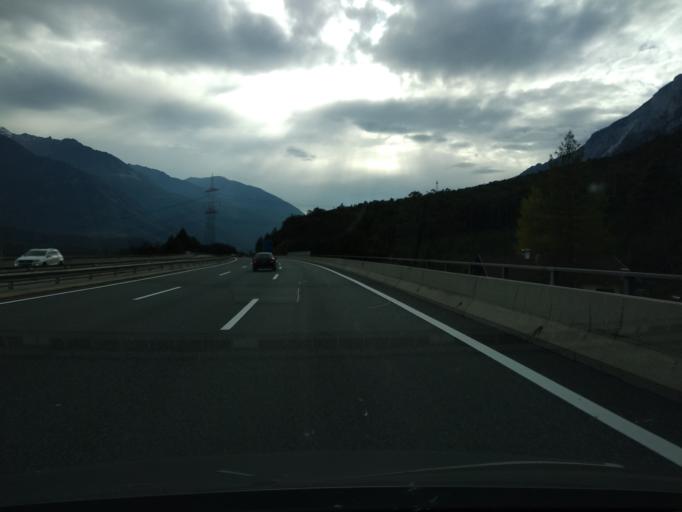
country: AT
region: Tyrol
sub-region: Politischer Bezirk Imst
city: Haiming
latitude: 47.2508
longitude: 10.8586
